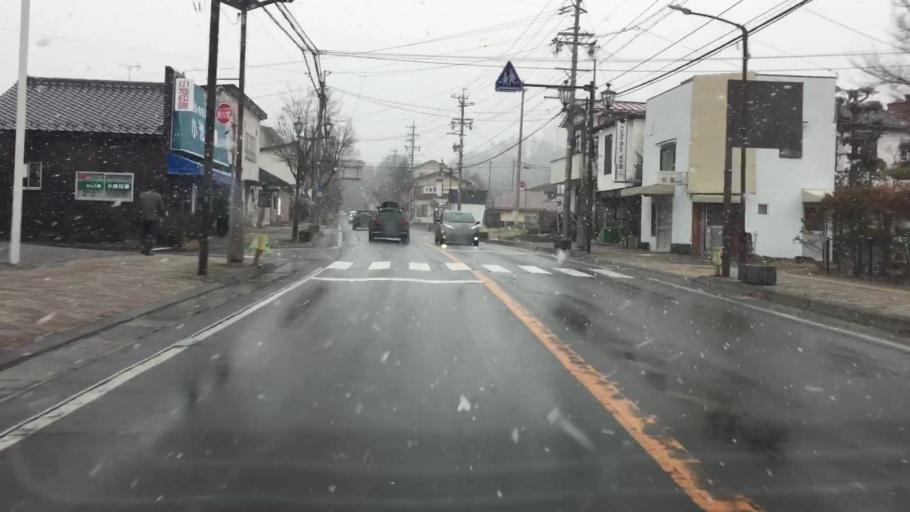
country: JP
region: Nagano
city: Komoro
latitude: 36.3507
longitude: 138.5915
